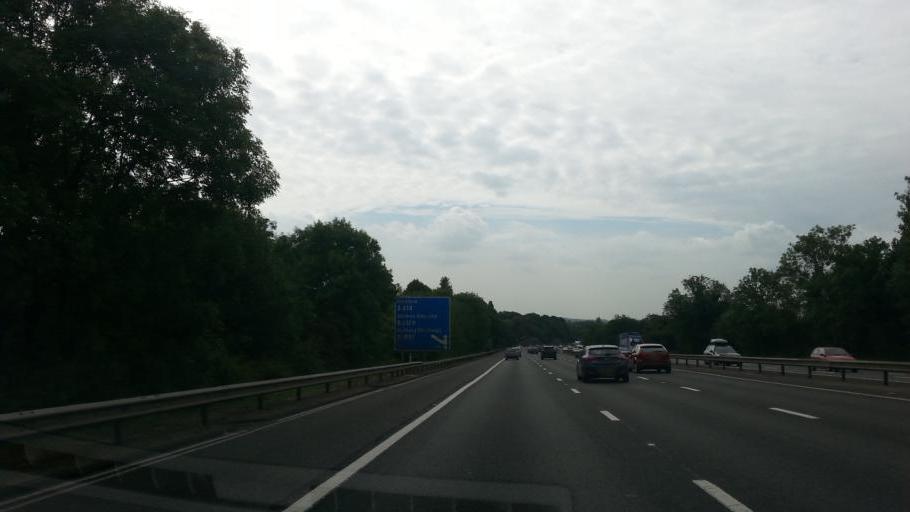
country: GB
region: England
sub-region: Hertfordshire
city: Welwyn Garden City
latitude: 51.7985
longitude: -0.2267
